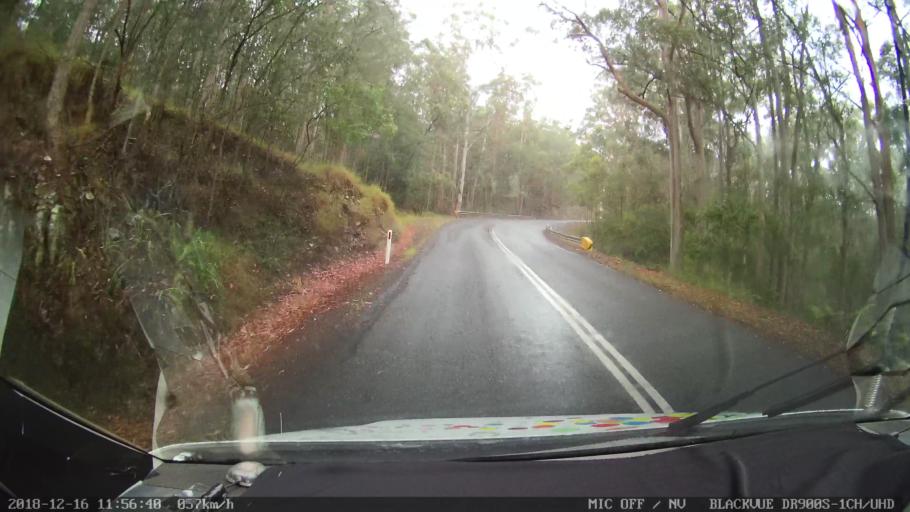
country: AU
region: New South Wales
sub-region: Tenterfield Municipality
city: Carrolls Creek
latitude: -28.9170
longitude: 152.3003
